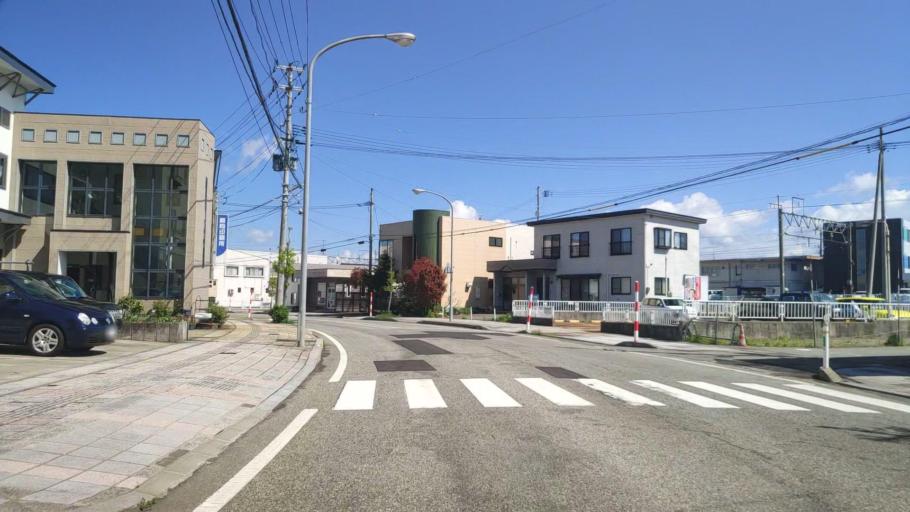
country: JP
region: Akita
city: Omagari
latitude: 39.4627
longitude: 140.4816
